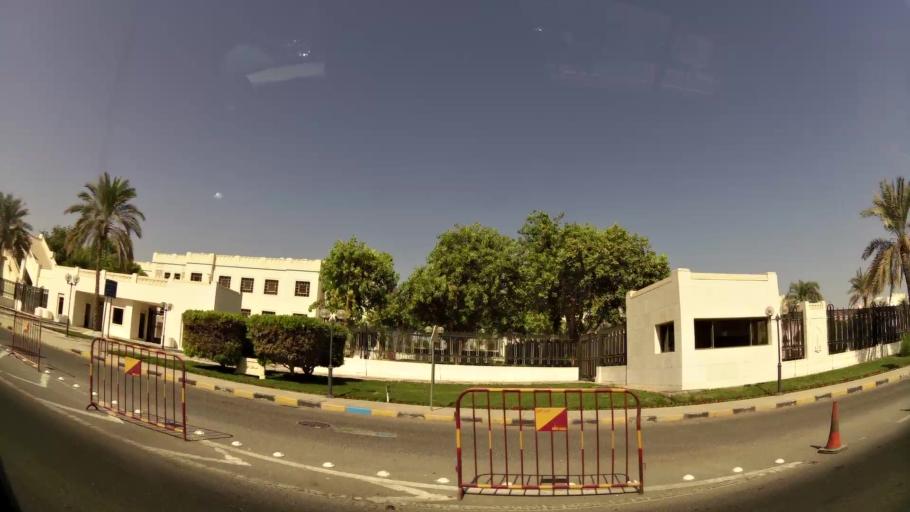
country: KW
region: Al Asimah
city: Kuwait City
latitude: 29.3773
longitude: 47.9696
